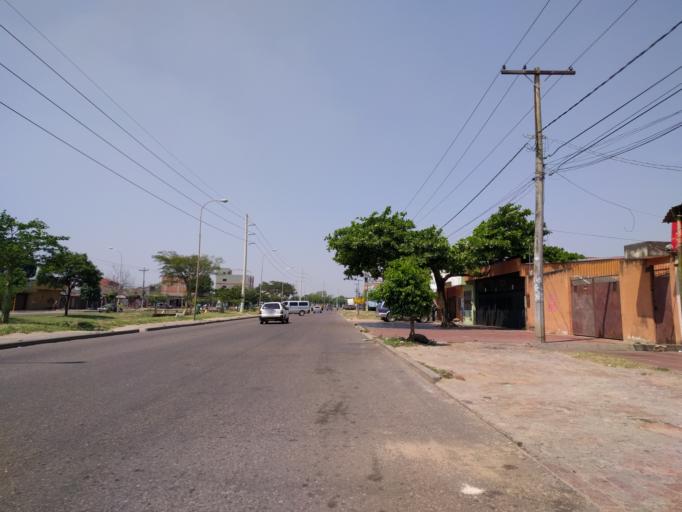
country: BO
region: Santa Cruz
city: Santa Cruz de la Sierra
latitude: -17.7944
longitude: -63.1490
